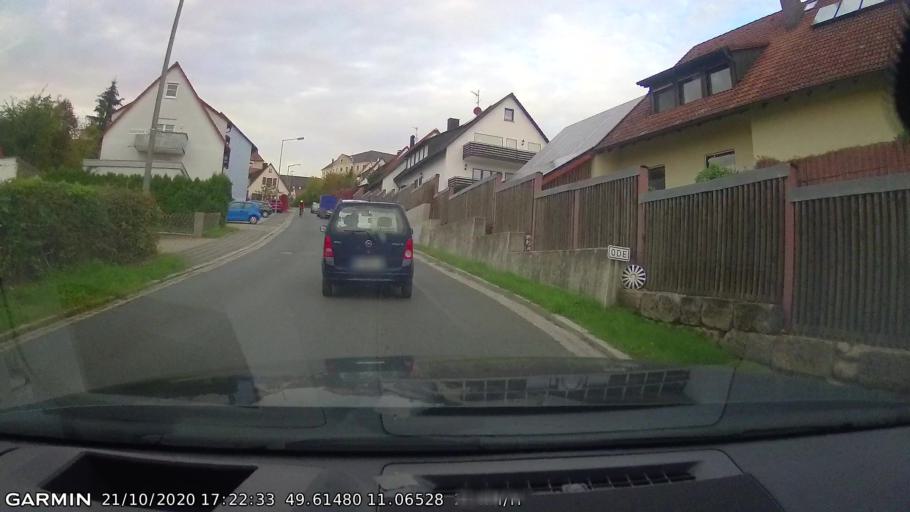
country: DE
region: Bavaria
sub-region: Regierungsbezirk Mittelfranken
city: Marloffstein
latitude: 49.6151
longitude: 11.0650
